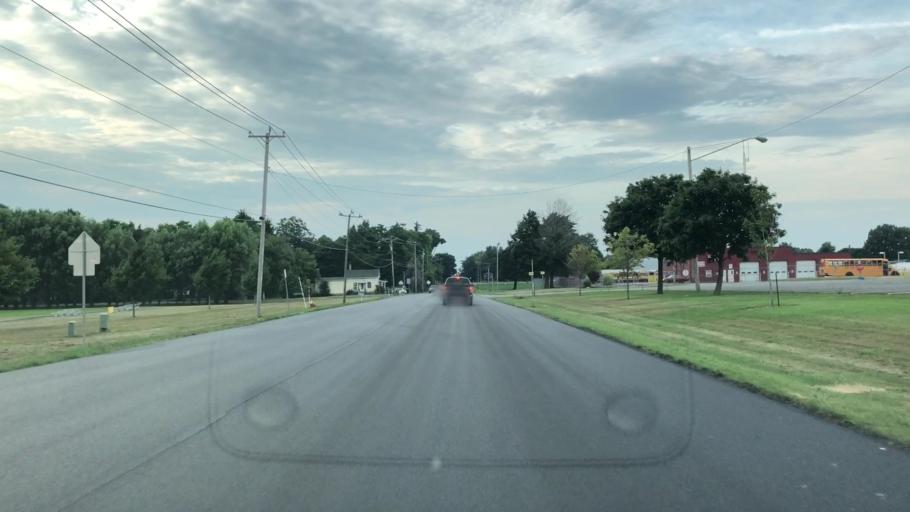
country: US
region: New York
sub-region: Erie County
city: Elma Center
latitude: 42.8359
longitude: -78.6060
